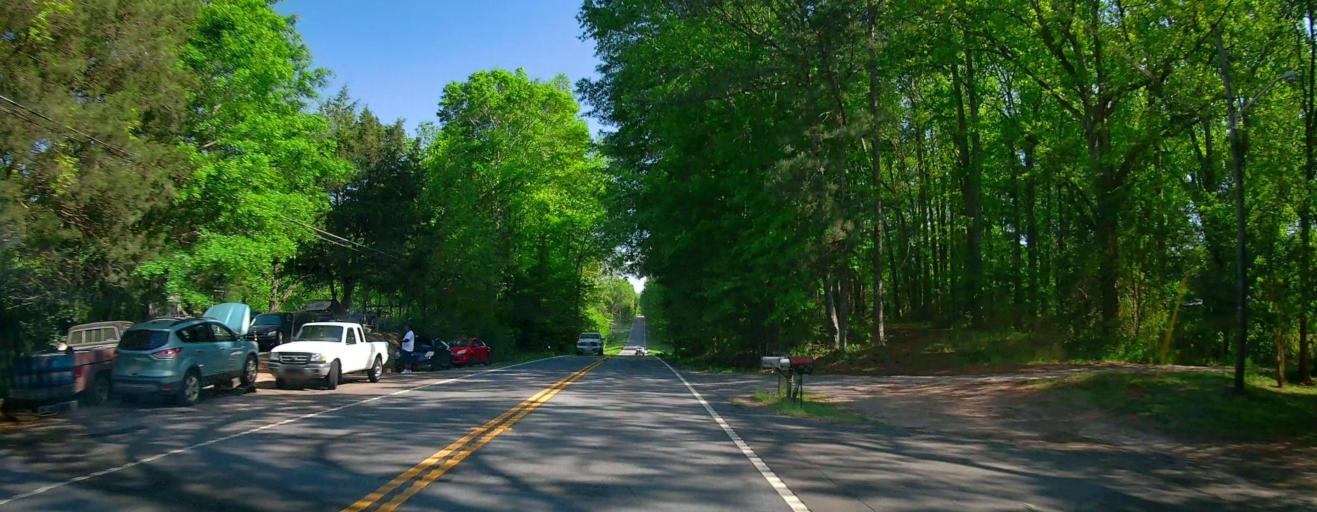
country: US
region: Georgia
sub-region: Morgan County
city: Madison
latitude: 33.6125
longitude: -83.4797
